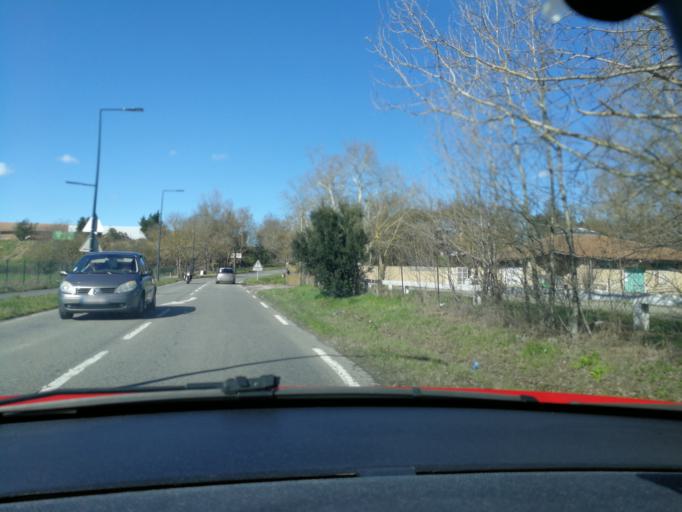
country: FR
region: Midi-Pyrenees
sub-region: Departement de la Haute-Garonne
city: Portet-sur-Garonne
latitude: 43.5419
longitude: 1.3900
